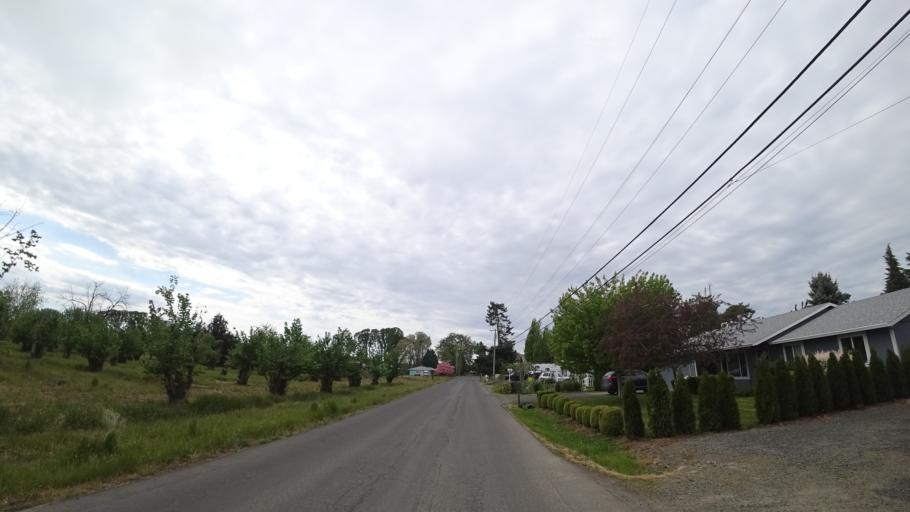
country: US
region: Oregon
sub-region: Washington County
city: Hillsboro
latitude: 45.4923
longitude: -122.9644
